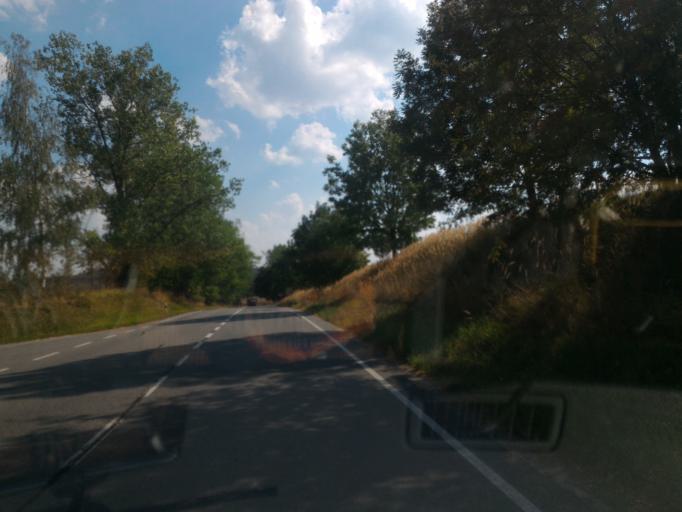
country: CZ
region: Vysocina
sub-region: Okres Jihlava
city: Trest'
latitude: 49.2678
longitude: 15.4764
